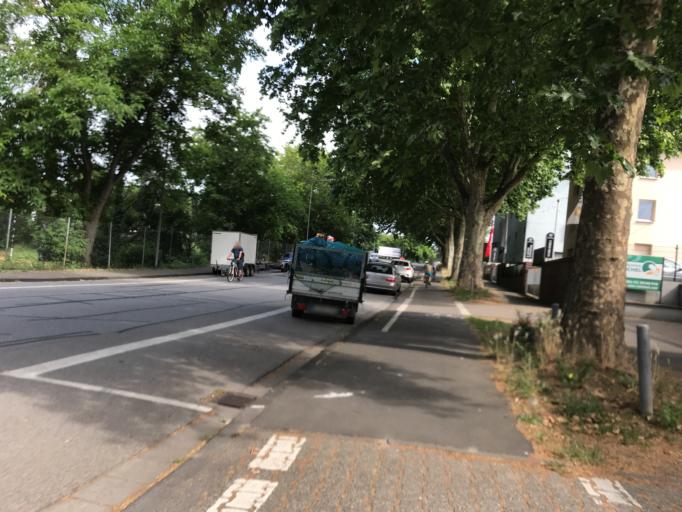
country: DE
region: Rheinland-Pfalz
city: Budenheim
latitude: 50.0462
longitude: 8.2046
